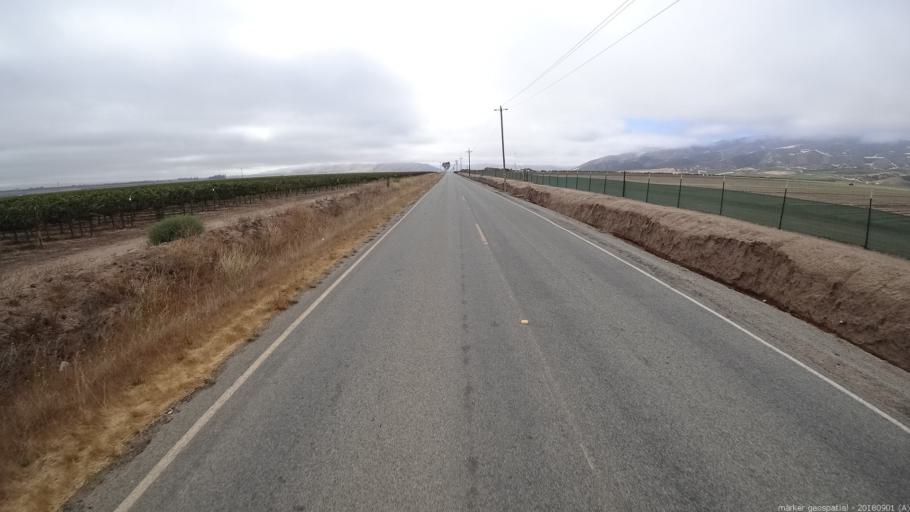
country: US
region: California
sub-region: Monterey County
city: Soledad
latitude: 36.3467
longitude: -121.3200
